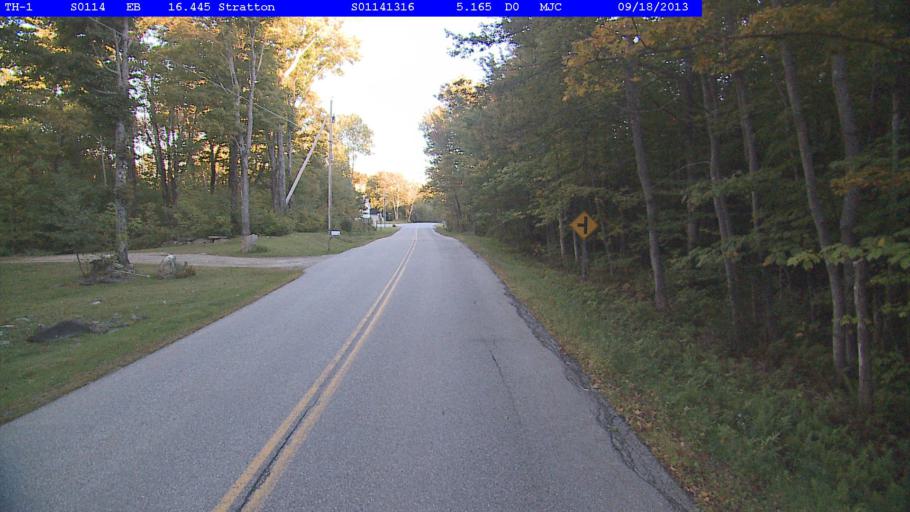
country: US
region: Vermont
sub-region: Windham County
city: Dover
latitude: 43.0436
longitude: -72.9110
